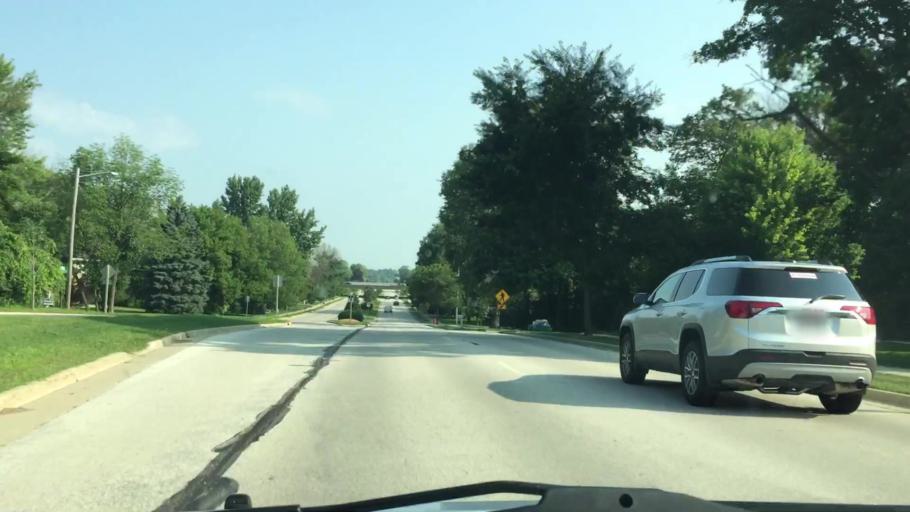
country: US
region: Wisconsin
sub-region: Waukesha County
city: Brookfield
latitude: 43.0237
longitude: -88.1269
